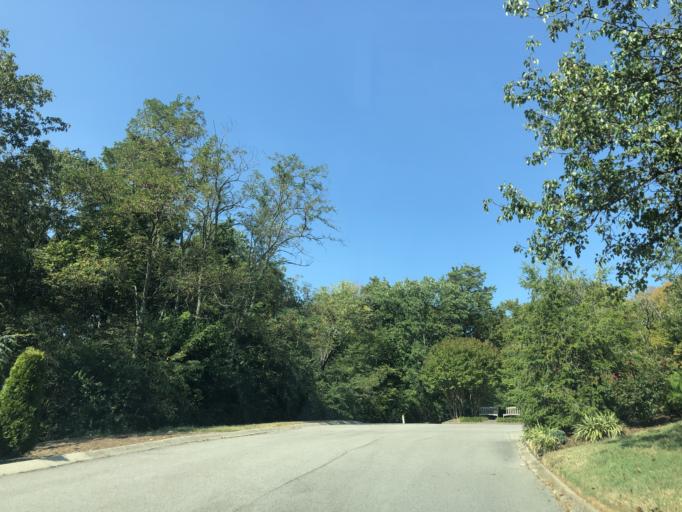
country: US
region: Tennessee
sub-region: Davidson County
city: Oak Hill
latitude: 36.0927
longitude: -86.8133
